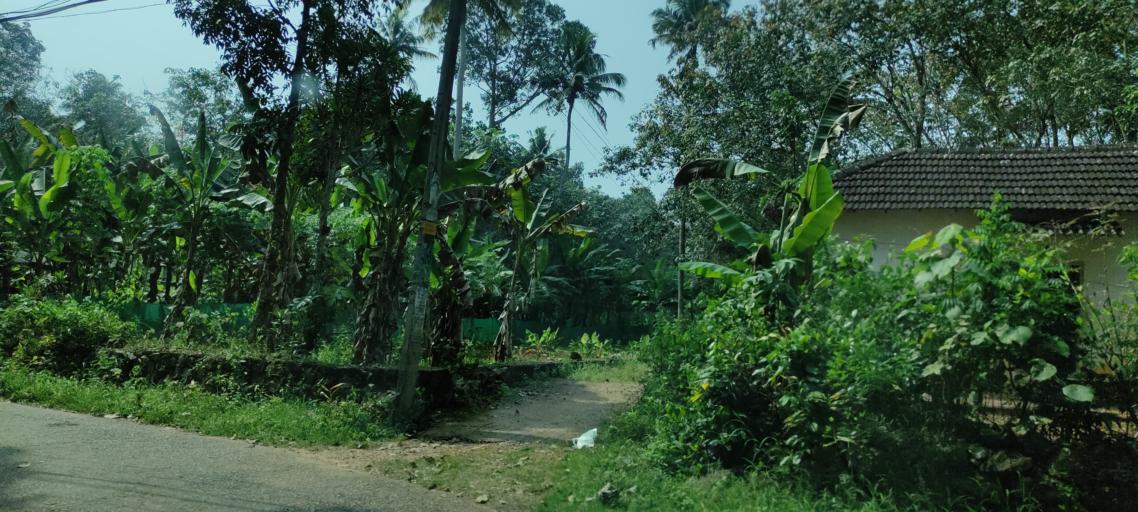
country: IN
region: Kerala
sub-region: Pattanamtitta
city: Adur
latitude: 9.2124
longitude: 76.6954
